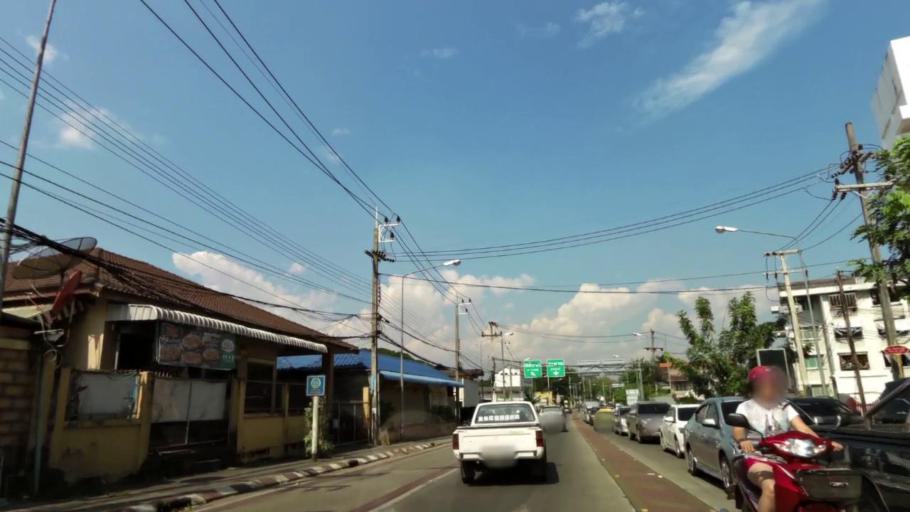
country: TH
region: Chiang Rai
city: Chiang Rai
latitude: 19.9131
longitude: 99.8324
